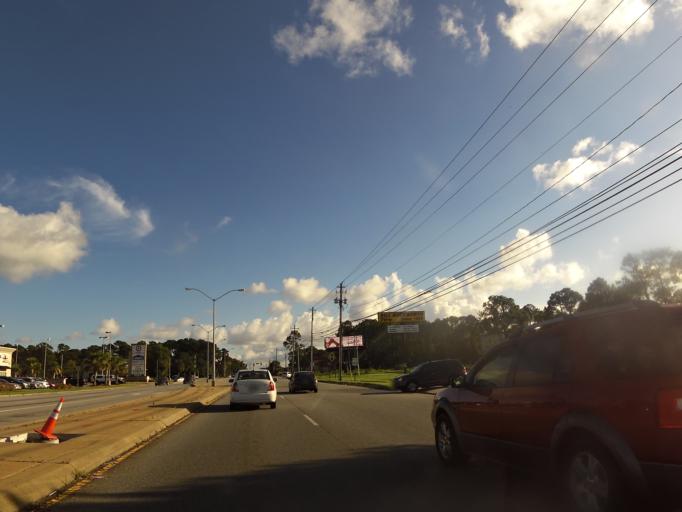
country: US
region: Georgia
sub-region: Glynn County
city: Country Club Estates
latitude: 31.2039
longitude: -81.4833
